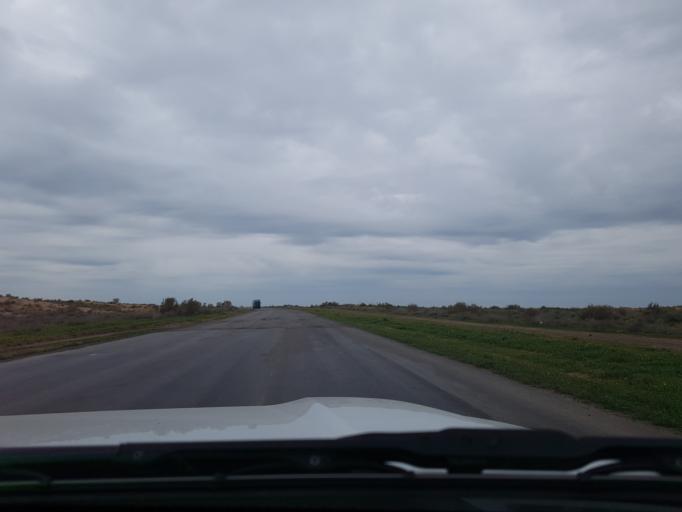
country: TM
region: Mary
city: Bayramaly
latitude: 37.6695
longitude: 62.3939
